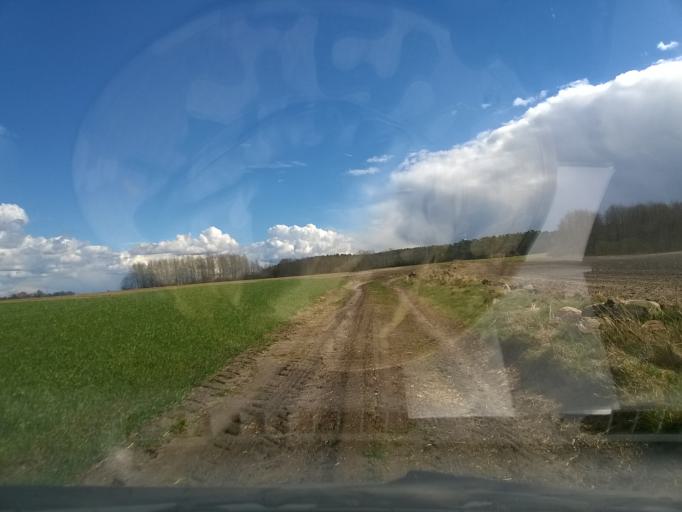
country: PL
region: Kujawsko-Pomorskie
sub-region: Powiat nakielski
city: Kcynia
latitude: 53.0358
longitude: 17.4014
